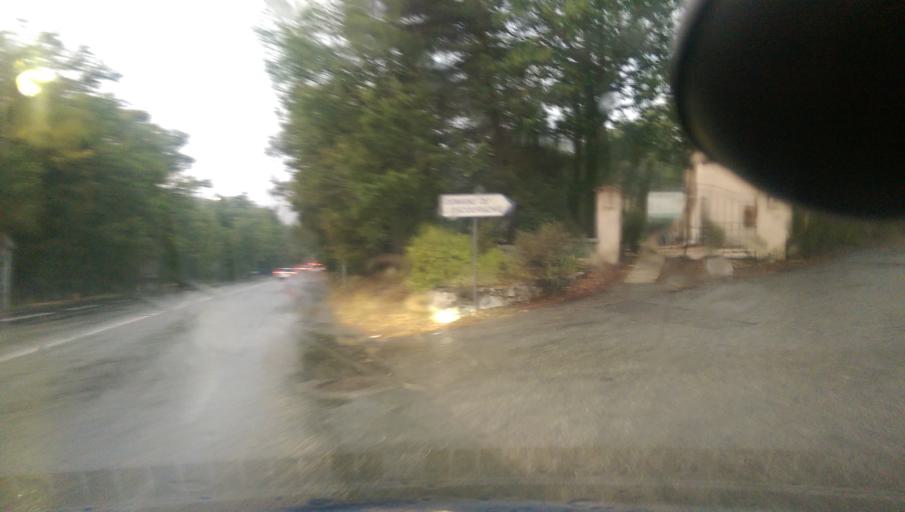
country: FR
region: Provence-Alpes-Cote d'Azur
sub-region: Departement des Alpes-Maritimes
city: Saint-Vallier-de-Thiey
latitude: 43.6916
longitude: 6.8624
